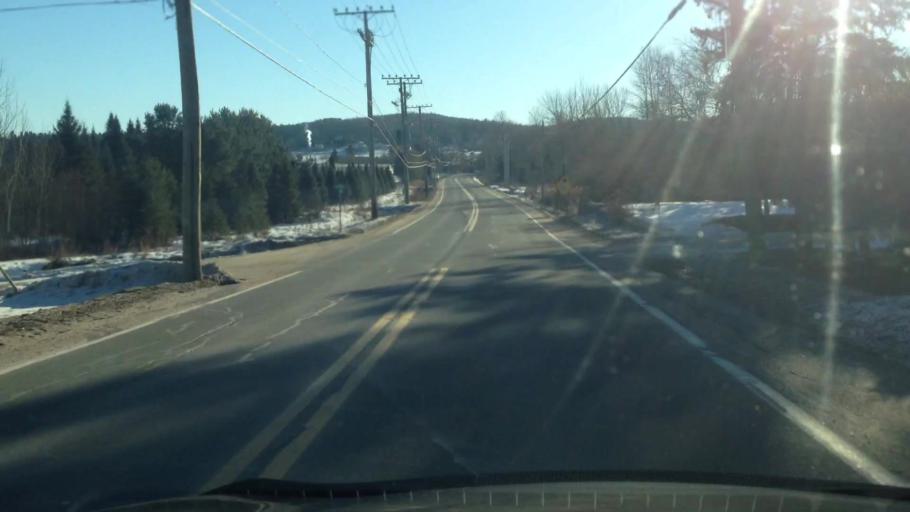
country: CA
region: Quebec
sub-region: Laurentides
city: Mont-Tremblant
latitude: 45.9747
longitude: -74.6147
